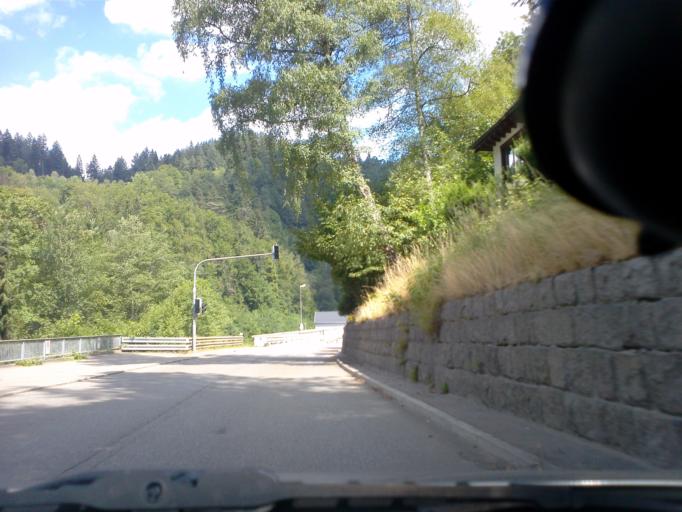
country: DE
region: Baden-Wuerttemberg
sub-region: Freiburg Region
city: Triberg im Schwarzwald
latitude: 48.1408
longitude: 8.2384
